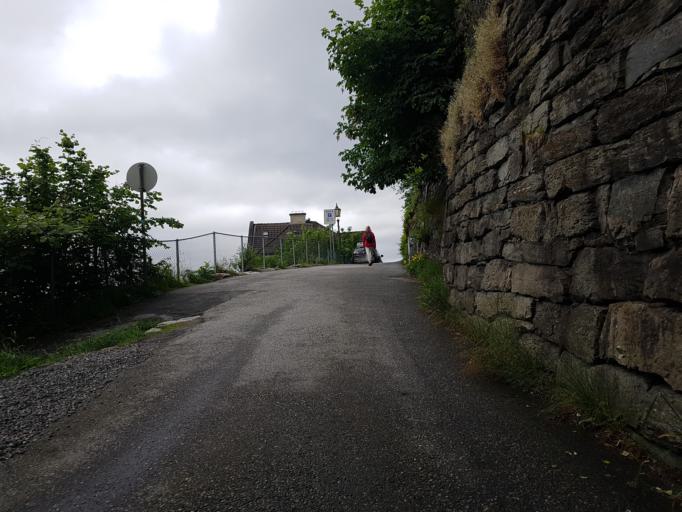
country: NO
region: Hordaland
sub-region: Bergen
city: Bergen
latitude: 60.3964
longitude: 5.3306
